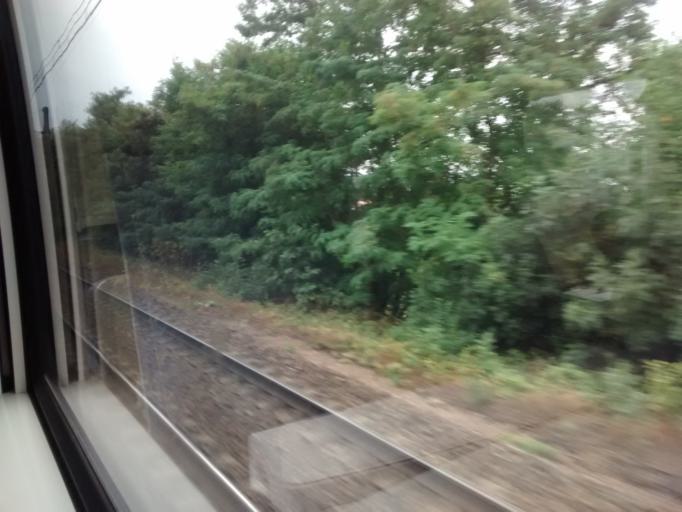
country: FR
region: Rhone-Alpes
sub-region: Departement du Rhone
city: Anse
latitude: 45.9377
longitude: 4.7222
